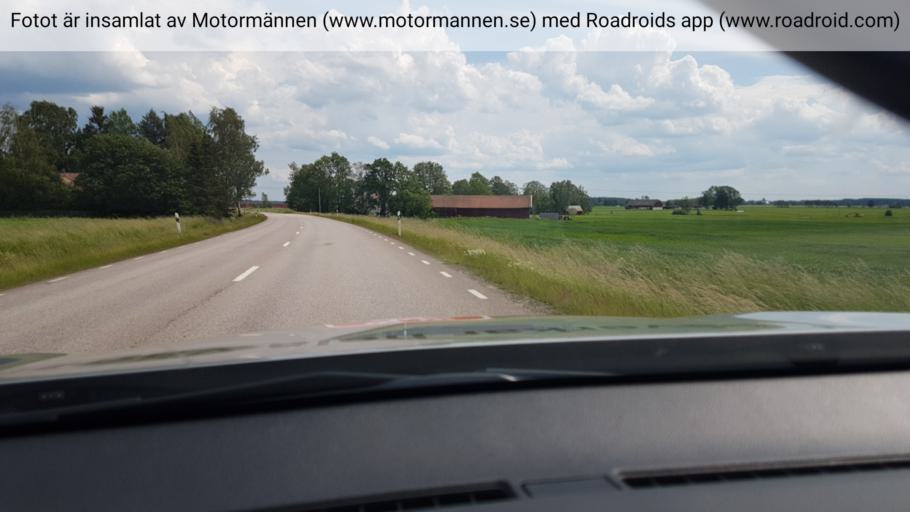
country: SE
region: Vaestra Goetaland
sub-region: Skovde Kommun
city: Skoevde
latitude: 58.3847
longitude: 13.9446
